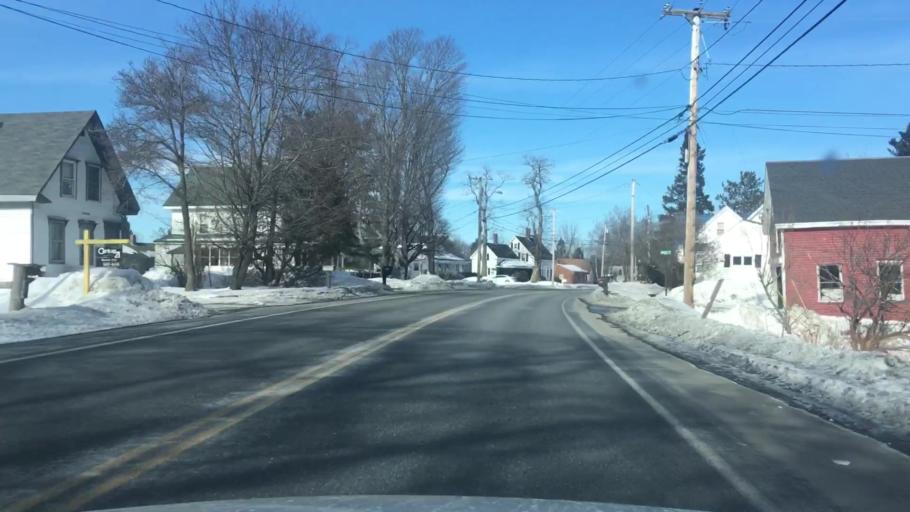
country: US
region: Maine
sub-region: Penobscot County
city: Orrington
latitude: 44.7479
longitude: -68.8071
